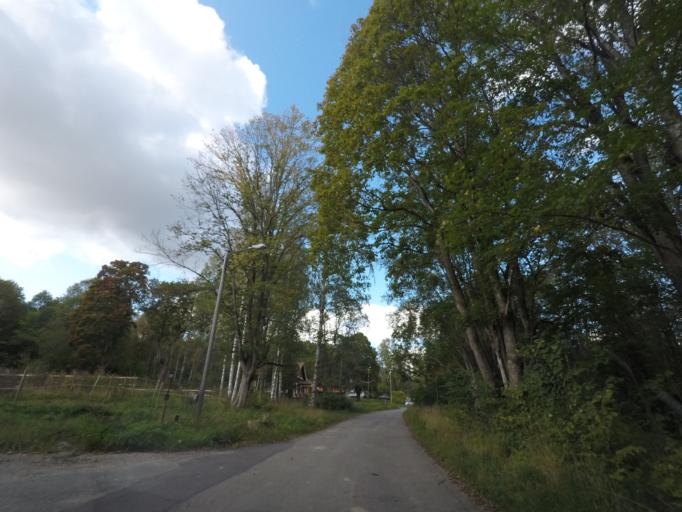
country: SE
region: Vaestmanland
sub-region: Skinnskattebergs Kommun
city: Skinnskatteberg
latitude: 59.8262
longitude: 15.6766
